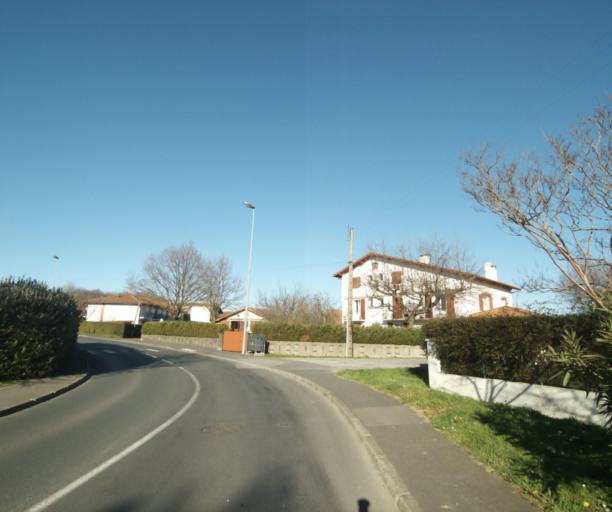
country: FR
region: Aquitaine
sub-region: Departement des Pyrenees-Atlantiques
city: Hendaye
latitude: 43.3660
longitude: -1.7570
